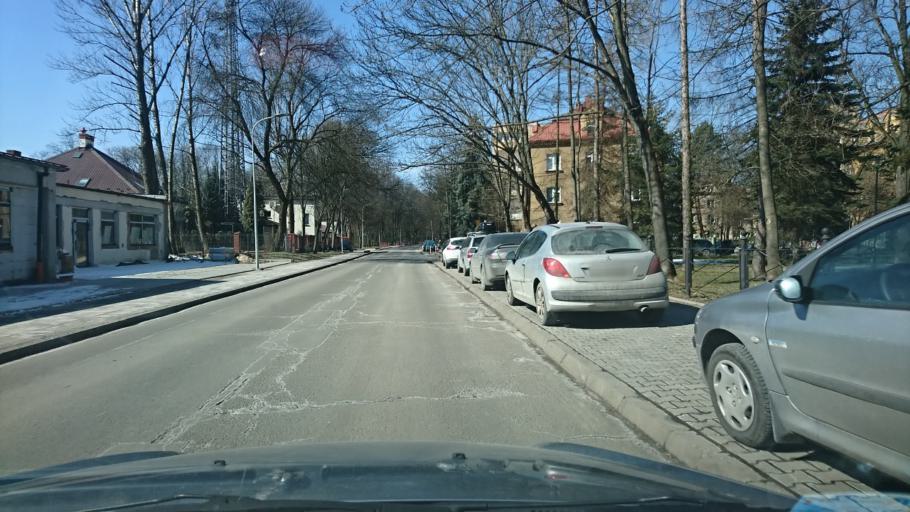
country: PL
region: Lesser Poland Voivodeship
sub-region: Powiat wielicki
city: Kokotow
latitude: 50.0662
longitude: 20.0508
